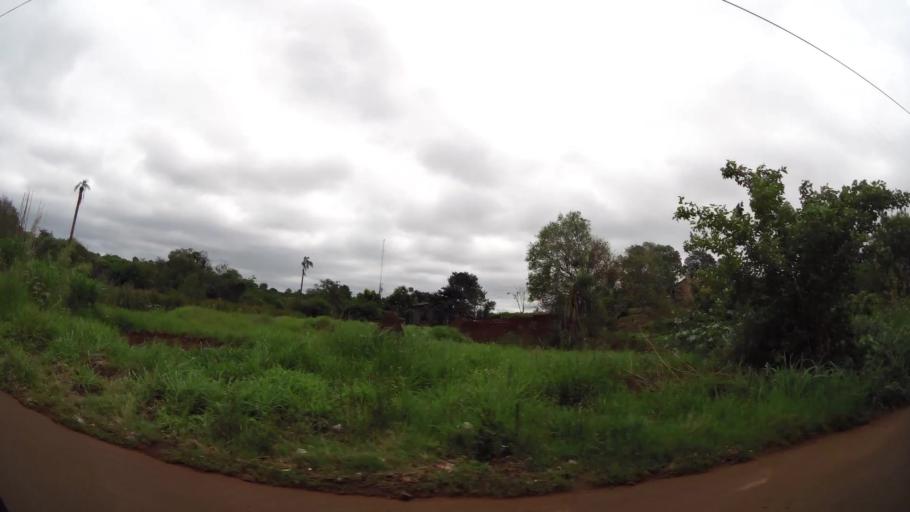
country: PY
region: Alto Parana
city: Ciudad del Este
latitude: -25.4994
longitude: -54.6877
